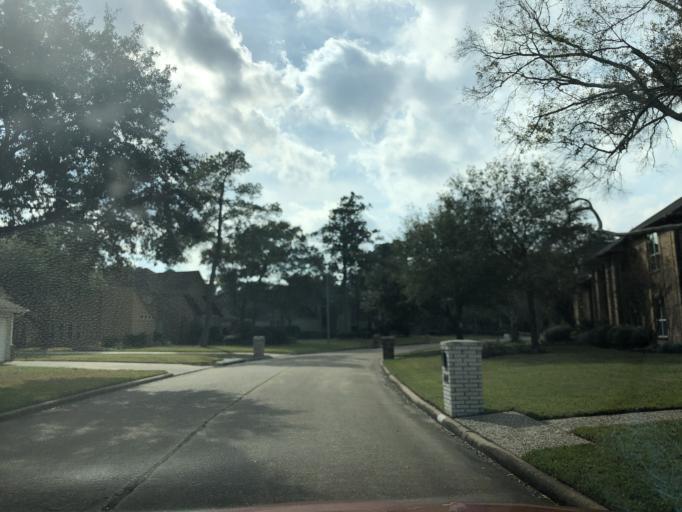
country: US
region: Texas
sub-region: Harris County
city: Tomball
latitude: 30.0316
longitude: -95.5361
